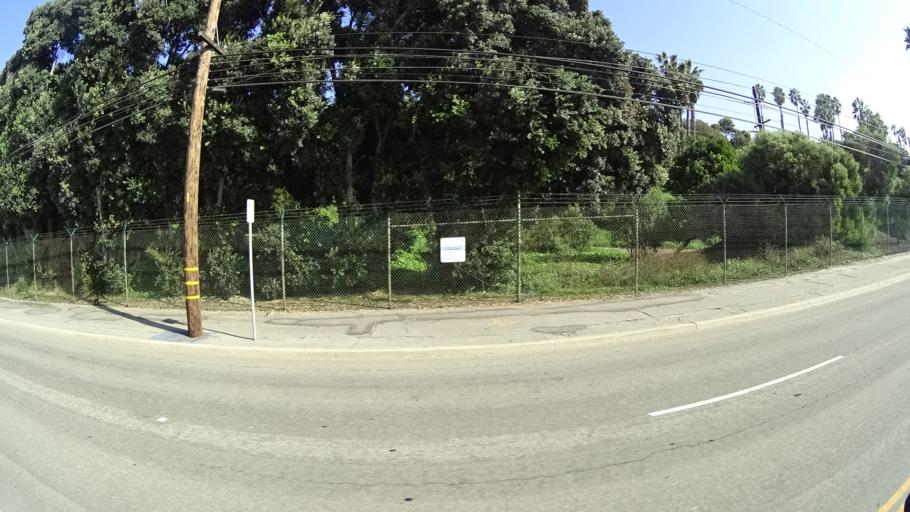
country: US
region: California
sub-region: Los Angeles County
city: El Segundo
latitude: 33.9141
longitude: -118.4264
